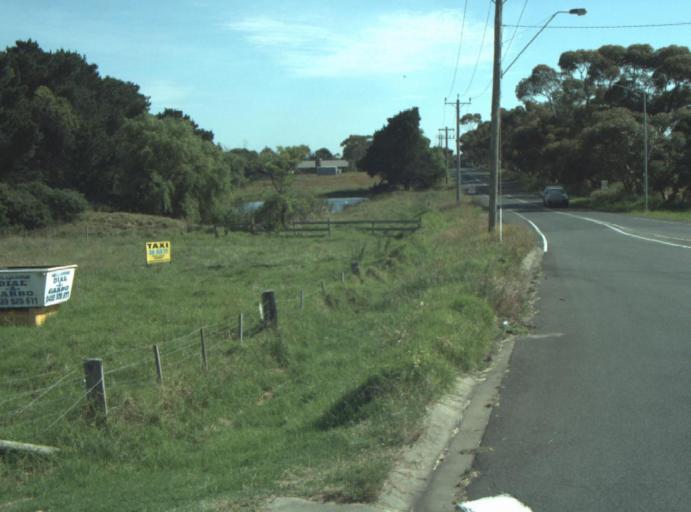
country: AU
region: Victoria
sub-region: Greater Geelong
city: Clifton Springs
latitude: -38.1849
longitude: 144.5499
